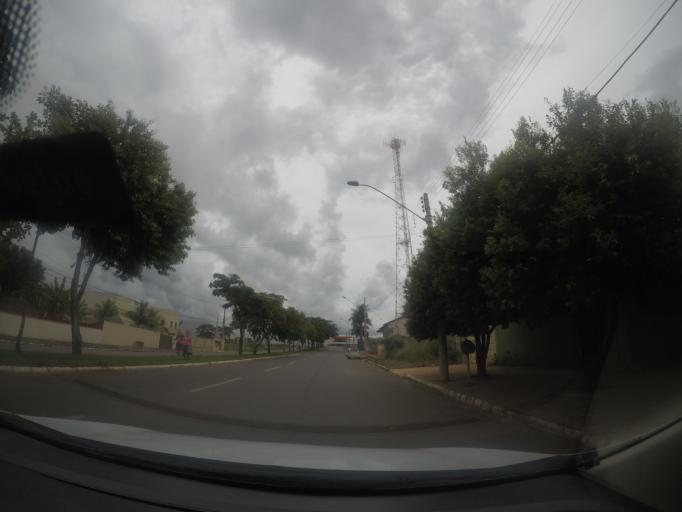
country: BR
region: Goias
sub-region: Trindade
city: Trindade
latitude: -16.6576
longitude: -49.3851
